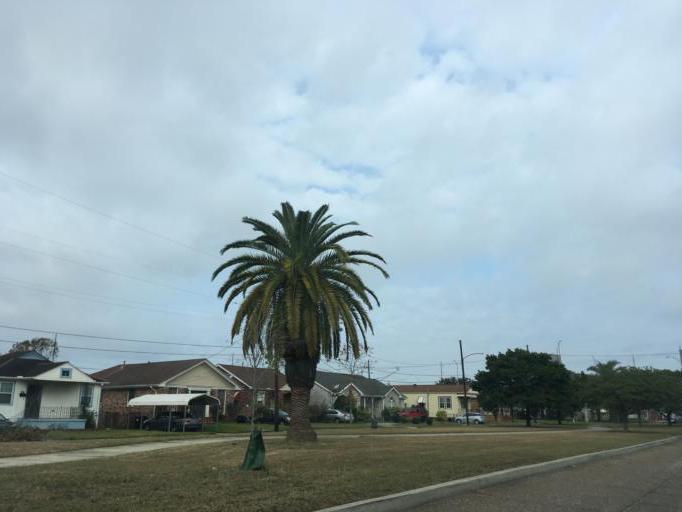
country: US
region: Louisiana
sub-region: Orleans Parish
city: New Orleans
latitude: 29.9895
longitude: -90.0631
